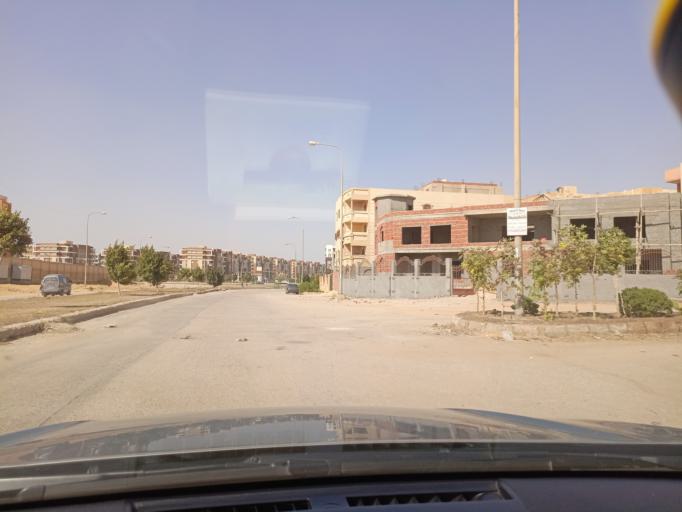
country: EG
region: Muhafazat al Qalyubiyah
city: Al Khankah
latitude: 30.2292
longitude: 31.4411
